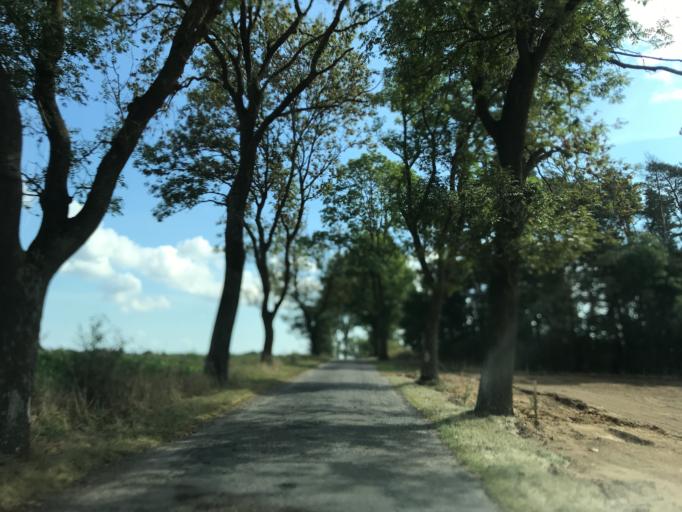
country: PL
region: Kujawsko-Pomorskie
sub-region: Powiat brodnicki
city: Brzozie
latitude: 53.3561
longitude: 19.6274
